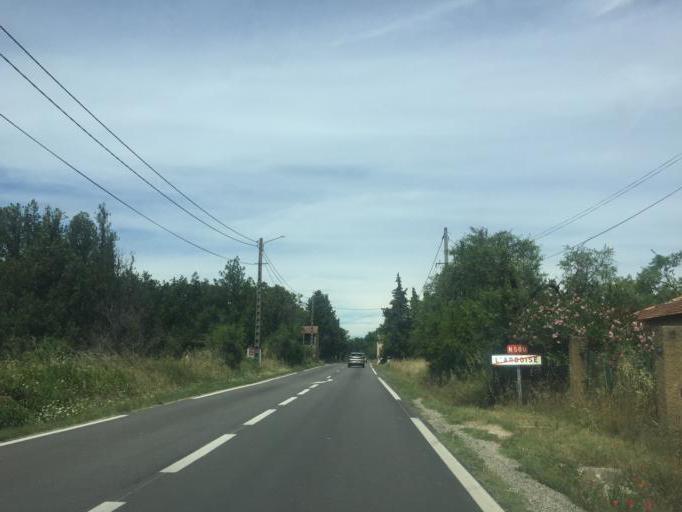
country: FR
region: Languedoc-Roussillon
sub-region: Departement du Gard
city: Laudun-l'Ardoise
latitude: 44.1096
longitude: 4.6919
